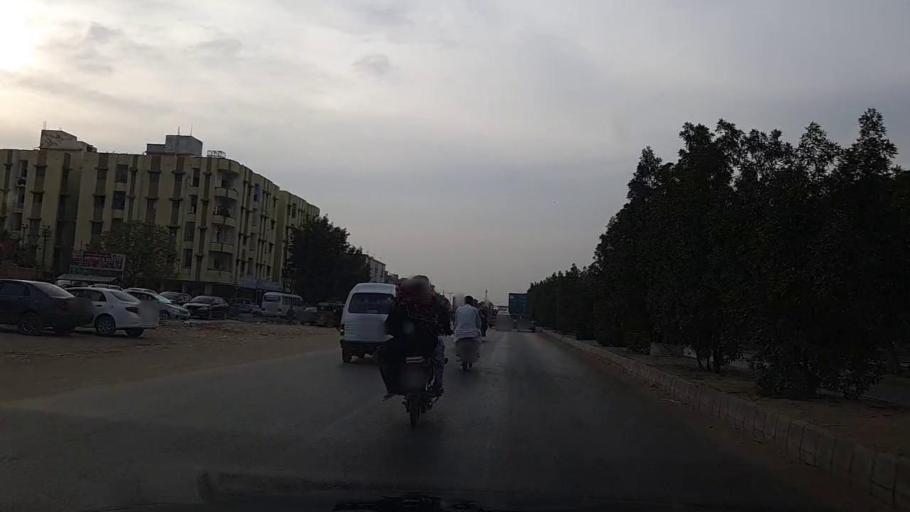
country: PK
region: Sindh
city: Malir Cantonment
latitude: 24.8601
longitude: 67.3340
